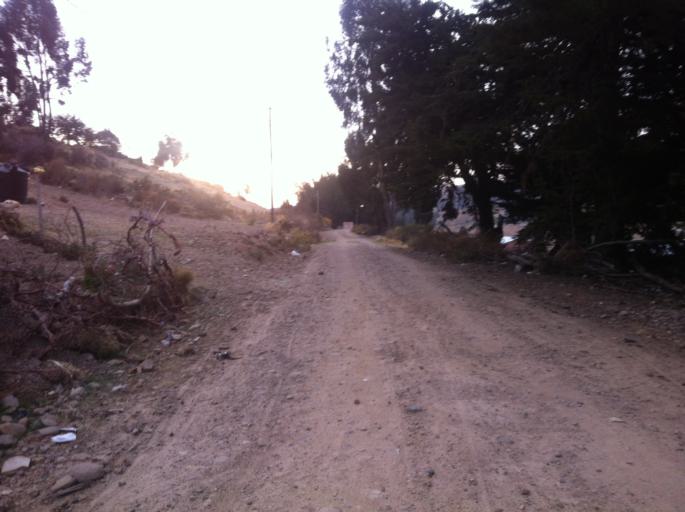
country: PE
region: Puno
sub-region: Yunguyo
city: Yunguyo
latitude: -16.1872
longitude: -69.0838
